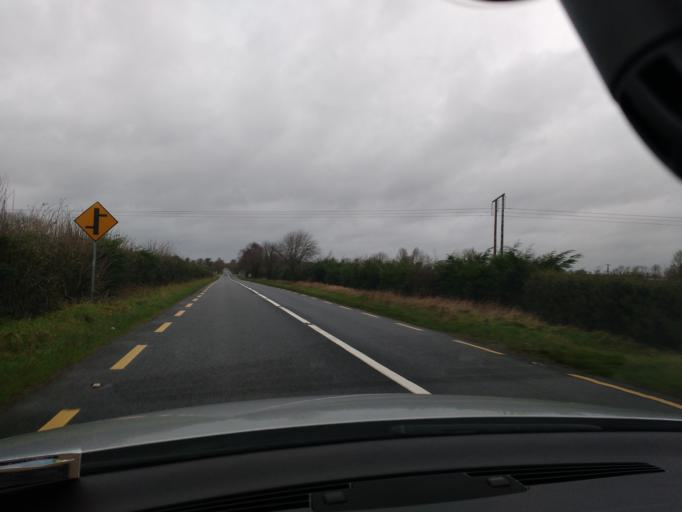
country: IE
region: Munster
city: Thurles
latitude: 52.6758
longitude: -7.7760
